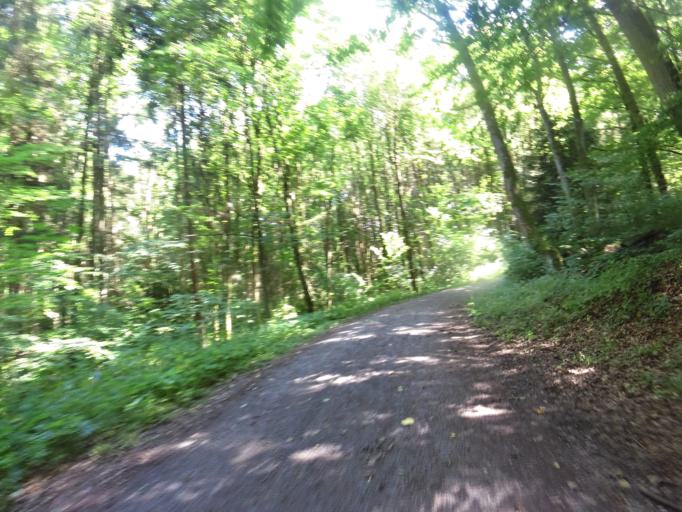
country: DE
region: Bavaria
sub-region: Regierungsbezirk Unterfranken
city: Gadheim
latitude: 49.8383
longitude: 9.9177
